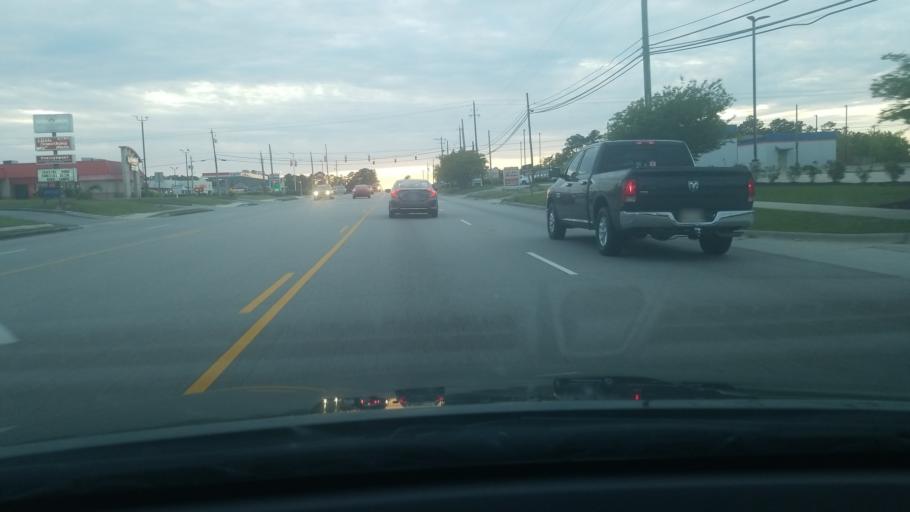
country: US
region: North Carolina
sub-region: Onslow County
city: Swansboro
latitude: 34.6926
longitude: -77.1288
